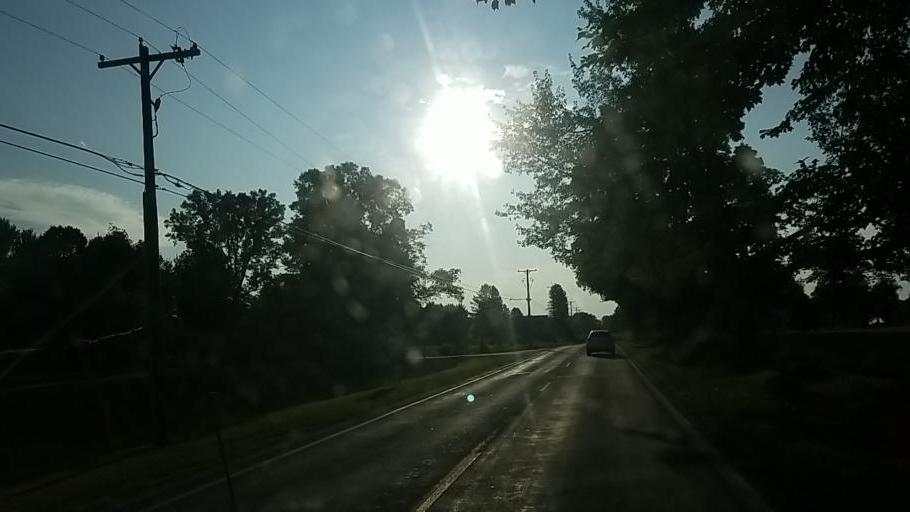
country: US
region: Michigan
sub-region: Montcalm County
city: Stanton
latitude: 43.2500
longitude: -85.1047
